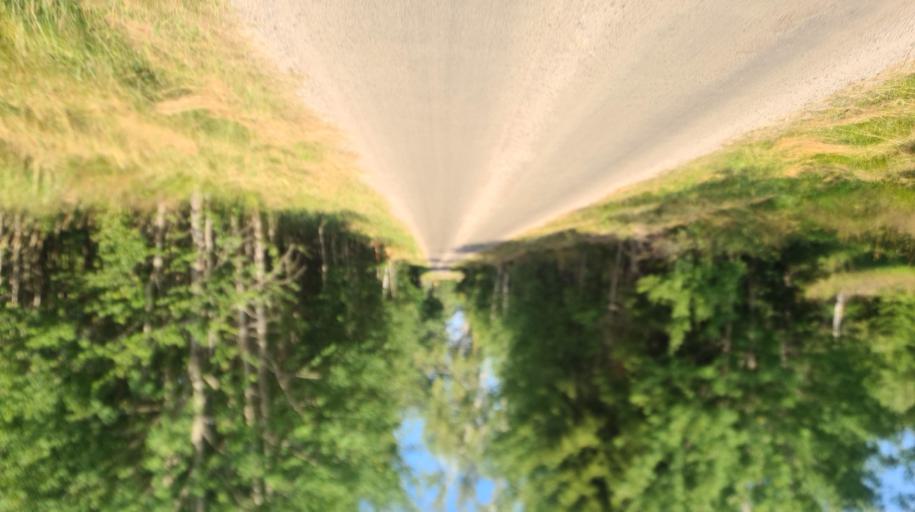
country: SE
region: Kronoberg
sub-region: Ljungby Kommun
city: Ljungby
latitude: 56.7223
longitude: 13.8843
